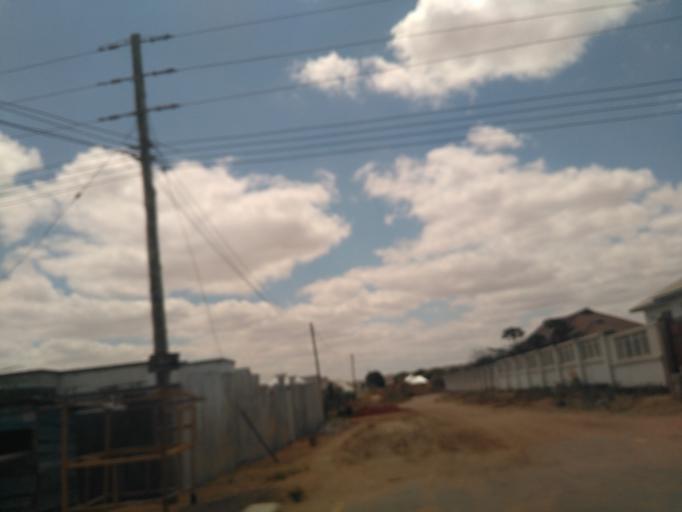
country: TZ
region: Dodoma
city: Kisasa
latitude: -6.1760
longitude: 35.7996
